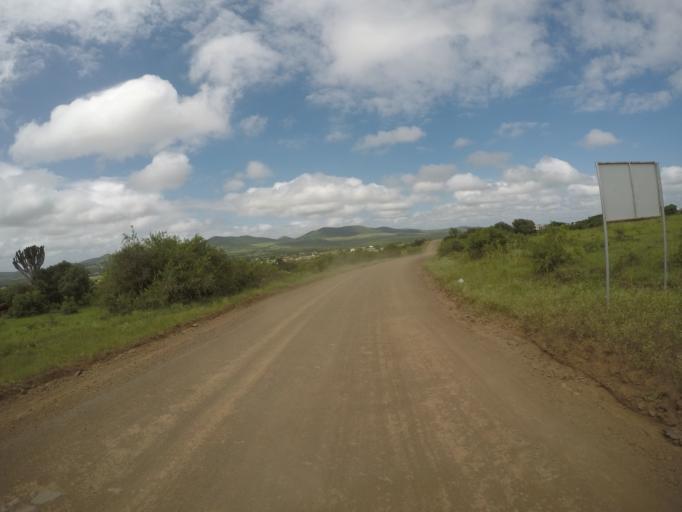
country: ZA
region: KwaZulu-Natal
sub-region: uThungulu District Municipality
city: Empangeni
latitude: -28.6049
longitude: 31.8489
